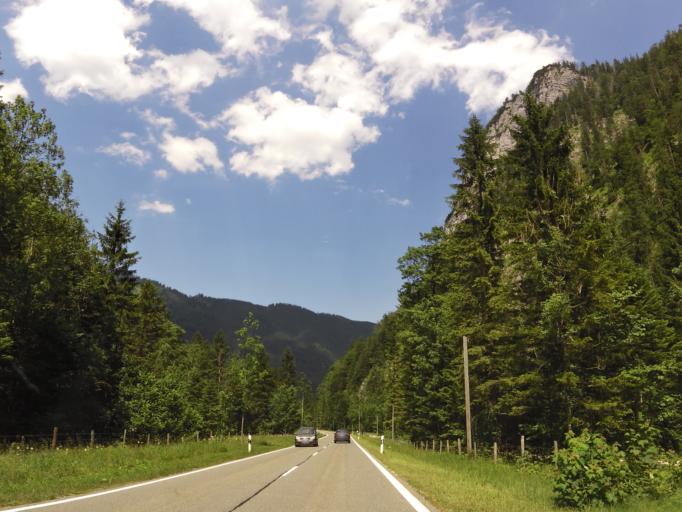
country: DE
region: Bavaria
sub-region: Upper Bavaria
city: Ruhpolding
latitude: 47.7022
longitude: 12.6160
